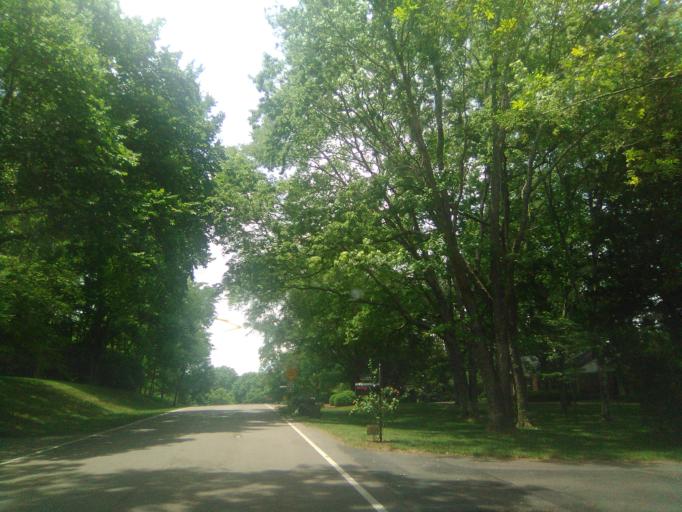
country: US
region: Tennessee
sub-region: Davidson County
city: Belle Meade
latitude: 36.0859
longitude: -86.8568
